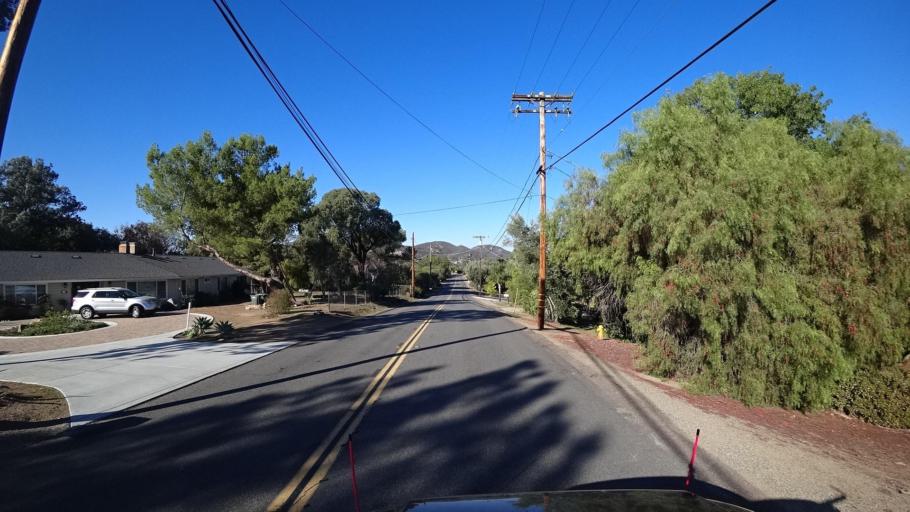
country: US
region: California
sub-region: San Diego County
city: Jamul
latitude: 32.7140
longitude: -116.8779
